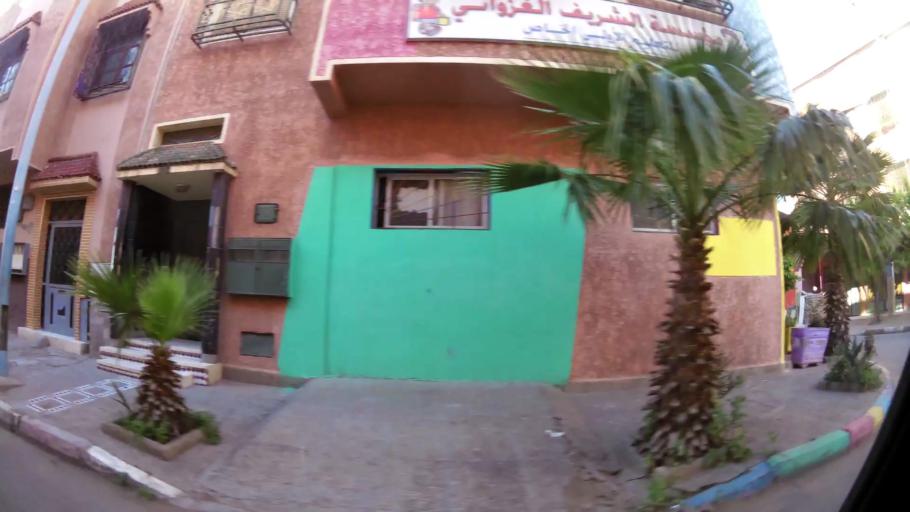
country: MA
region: Marrakech-Tensift-Al Haouz
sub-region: Marrakech
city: Marrakesh
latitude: 31.6203
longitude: -8.0656
